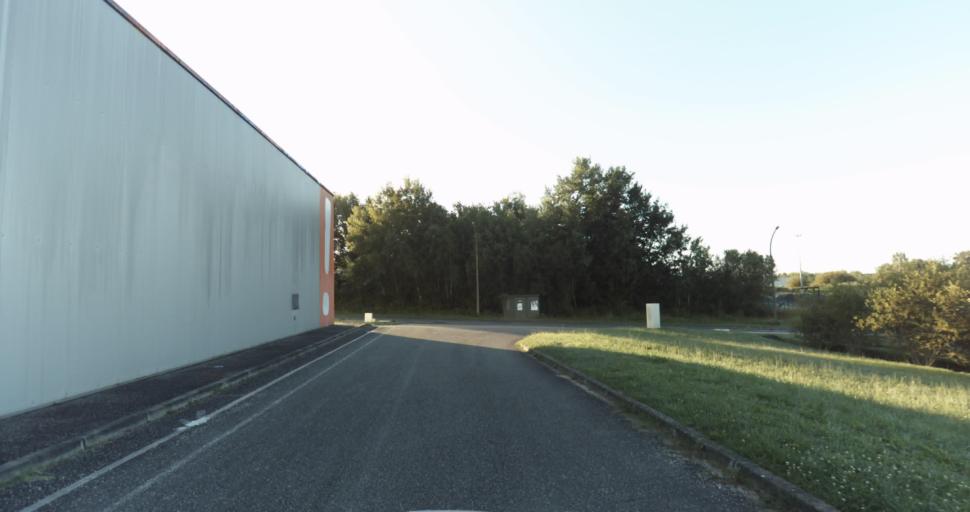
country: FR
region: Aquitaine
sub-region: Departement de la Gironde
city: Bazas
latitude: 44.4403
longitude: -0.2362
